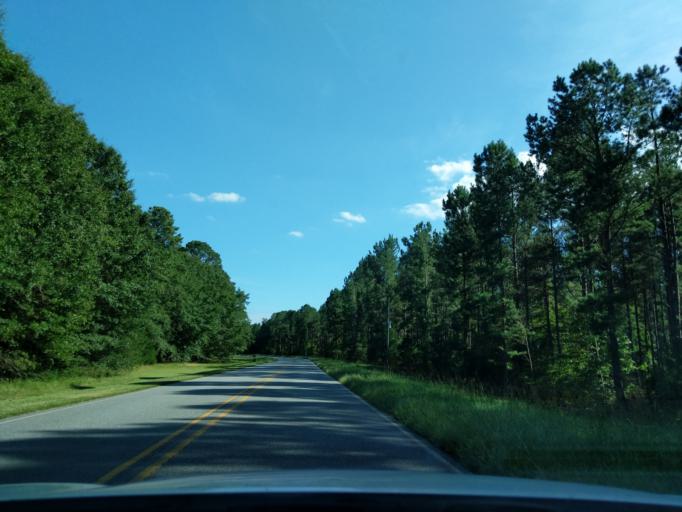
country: US
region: Georgia
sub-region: Oglethorpe County
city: Lexington
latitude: 33.9584
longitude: -83.0776
